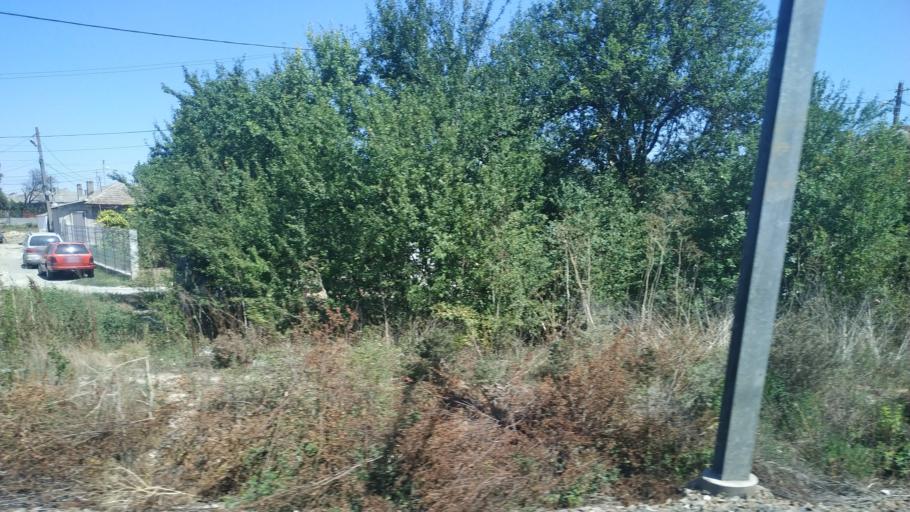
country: RO
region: Constanta
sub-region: Oras Murfatlar
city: Murfatlar
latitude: 44.1753
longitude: 28.4035
